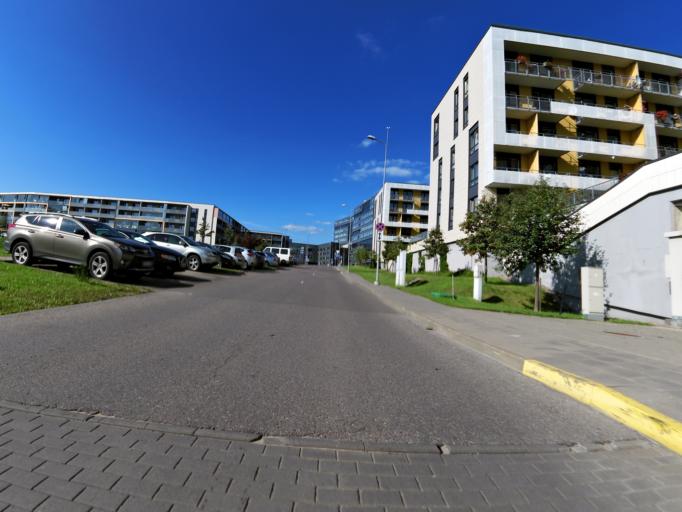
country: LT
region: Vilnius County
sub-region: Vilnius
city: Vilnius
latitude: 54.7180
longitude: 25.2851
